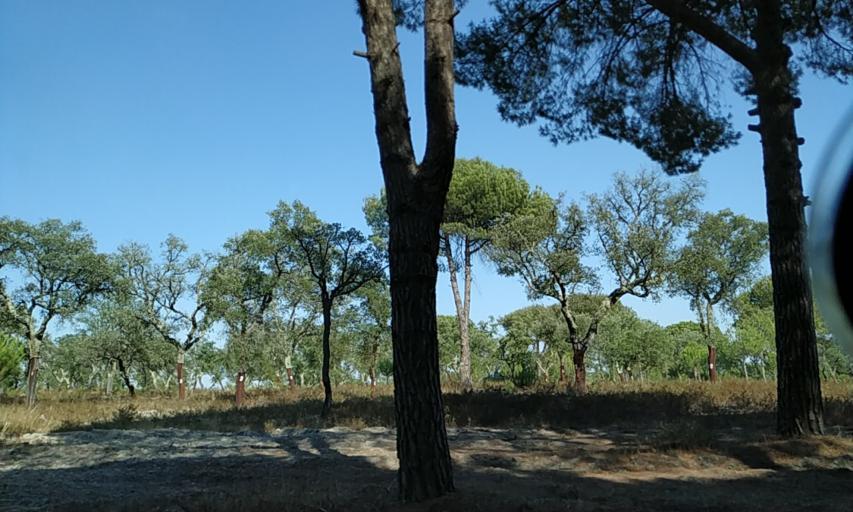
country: PT
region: Santarem
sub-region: Coruche
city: Coruche
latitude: 38.8381
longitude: -8.5574
